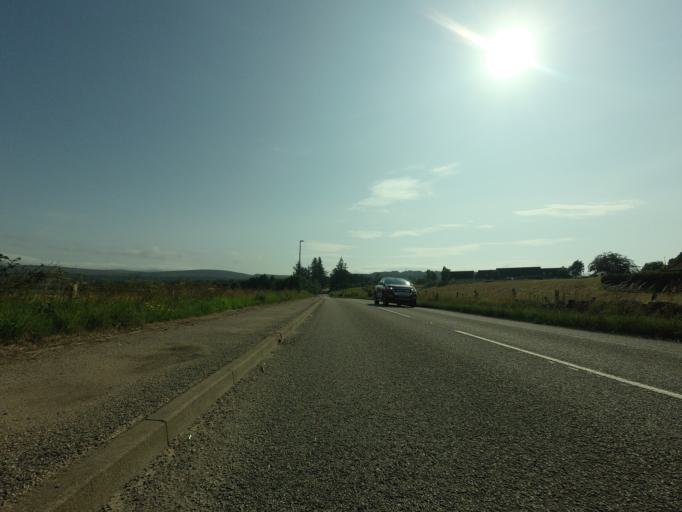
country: GB
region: Scotland
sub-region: Highland
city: Alness
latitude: 57.8847
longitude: -4.3606
